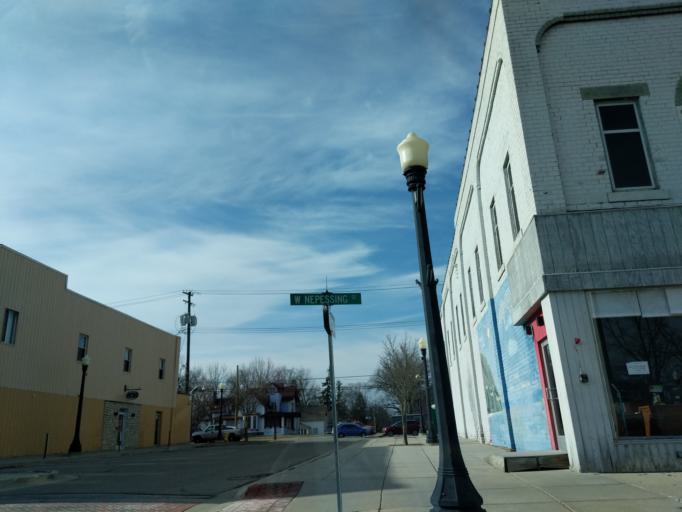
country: US
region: Michigan
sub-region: Lapeer County
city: Lapeer
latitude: 43.0542
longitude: -83.3116
